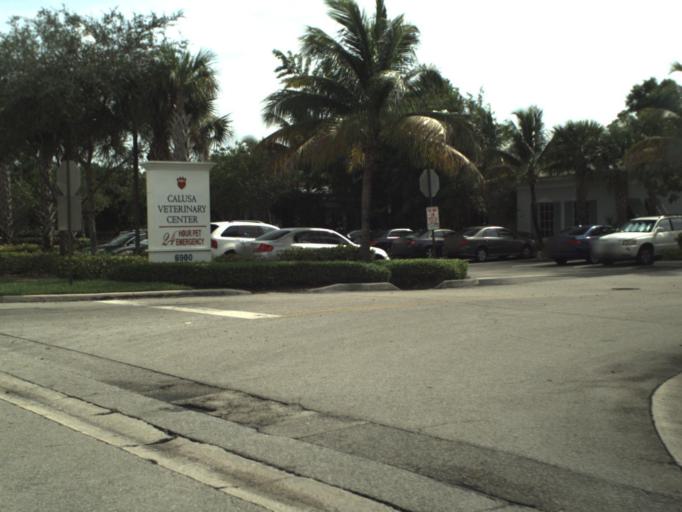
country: US
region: Florida
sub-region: Palm Beach County
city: Highland Beach
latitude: 26.4089
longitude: -80.1023
